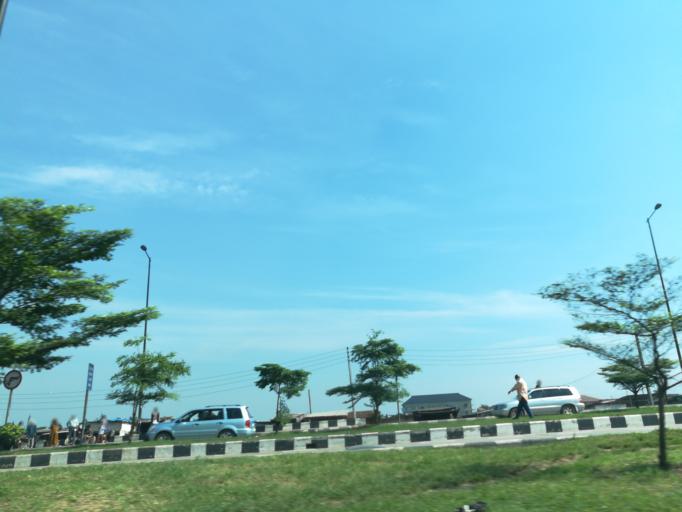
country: NG
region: Lagos
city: Ojota
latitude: 6.6095
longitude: 3.4305
